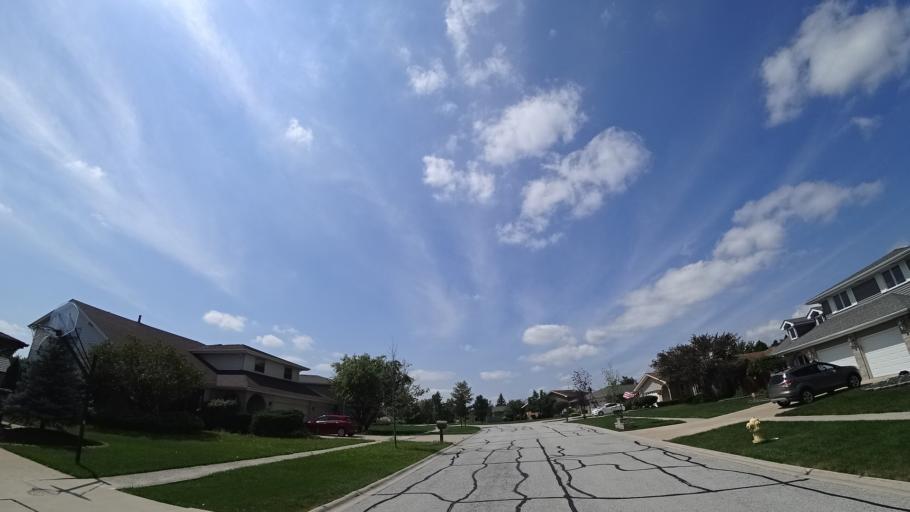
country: US
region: Illinois
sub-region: Cook County
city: Orland Hills
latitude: 41.5666
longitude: -87.8381
